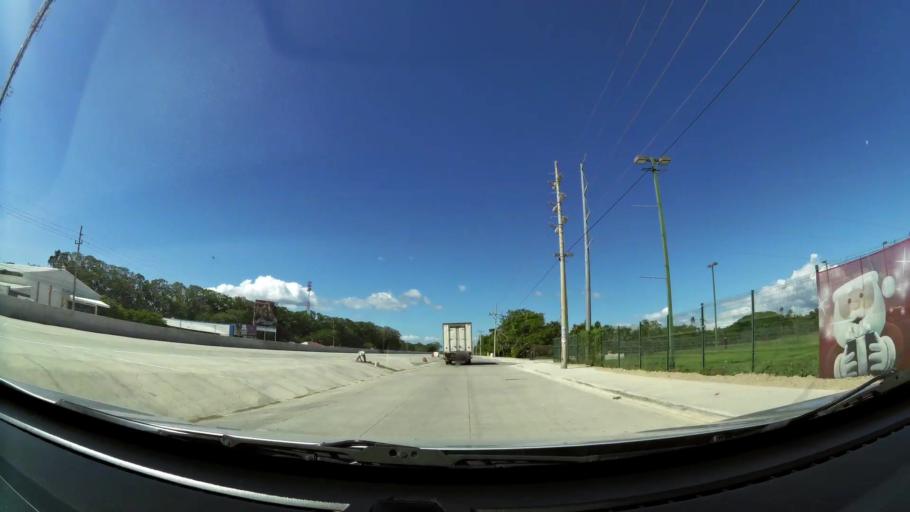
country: CR
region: Guanacaste
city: Liberia
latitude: 10.6182
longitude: -85.4380
